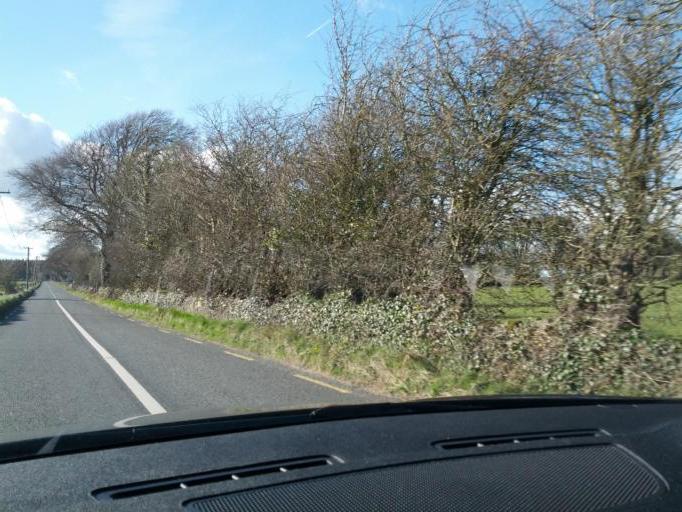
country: IE
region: Connaught
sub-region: Roscommon
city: Castlerea
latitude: 53.5451
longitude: -8.5526
